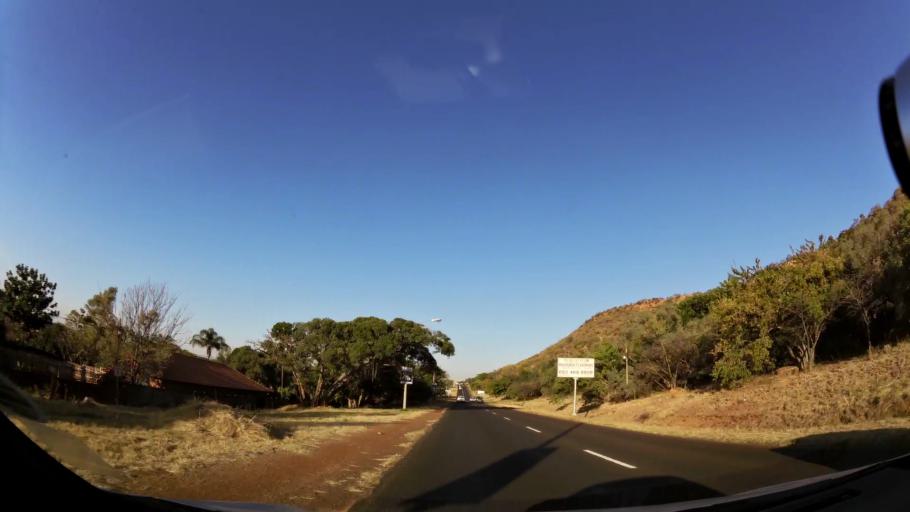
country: ZA
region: North-West
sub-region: Bojanala Platinum District Municipality
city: Rustenburg
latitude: -25.7026
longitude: 27.2276
